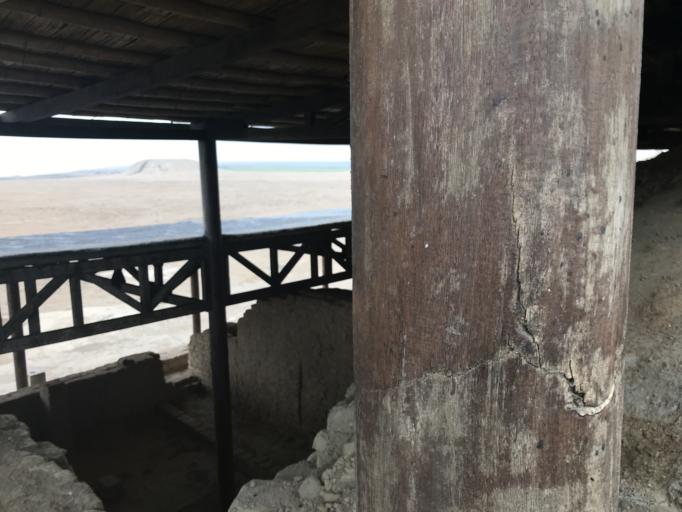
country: PE
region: La Libertad
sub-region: Ascope
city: Santiago de Cao
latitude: -7.9155
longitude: -79.3036
